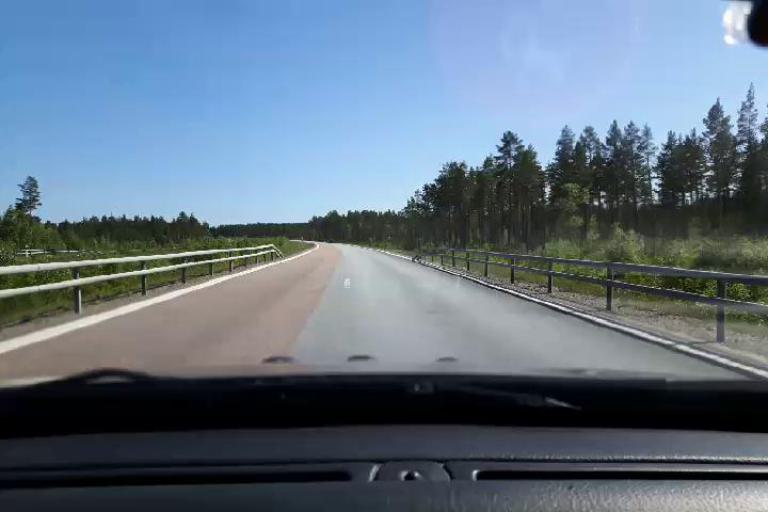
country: SE
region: Gaevleborg
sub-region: Soderhamns Kommun
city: Soderhamn
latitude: 61.3804
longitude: 16.9935
